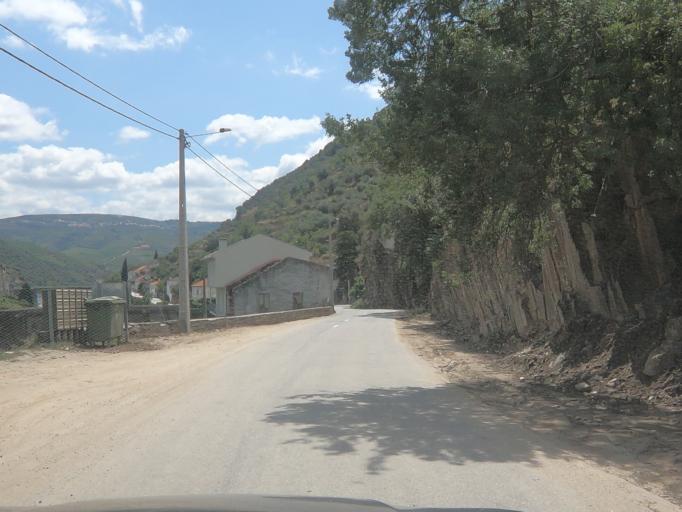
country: PT
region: Vila Real
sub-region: Sabrosa
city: Vilela
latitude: 41.1957
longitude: -7.5482
